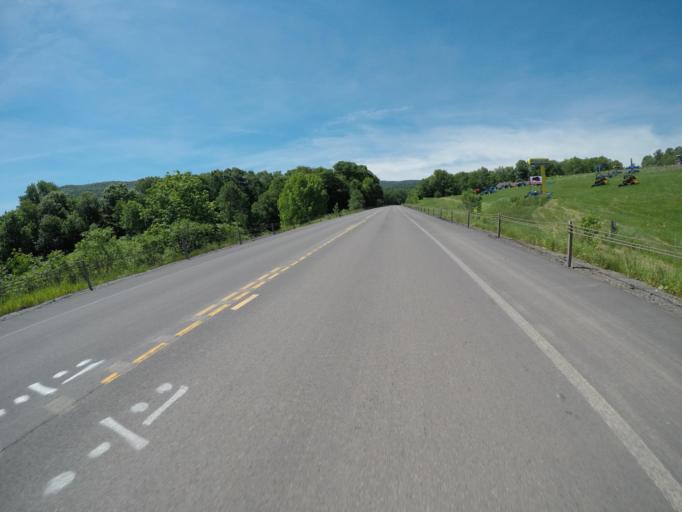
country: US
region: New York
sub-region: Delaware County
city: Walton
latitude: 42.1740
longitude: -75.0245
